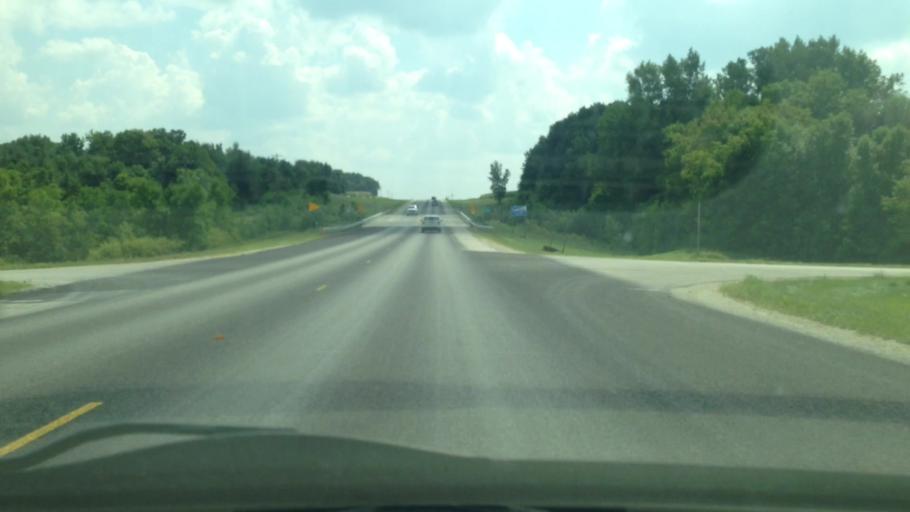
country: US
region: Minnesota
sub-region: Mower County
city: Grand Meadow
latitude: 43.7472
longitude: -92.4793
